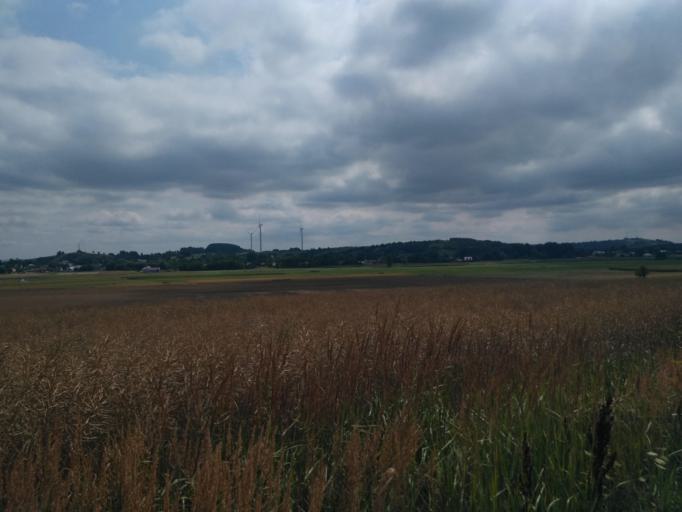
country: PL
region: Subcarpathian Voivodeship
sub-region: Powiat krosnienski
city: Rymanow
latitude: 49.6044
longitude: 21.8470
